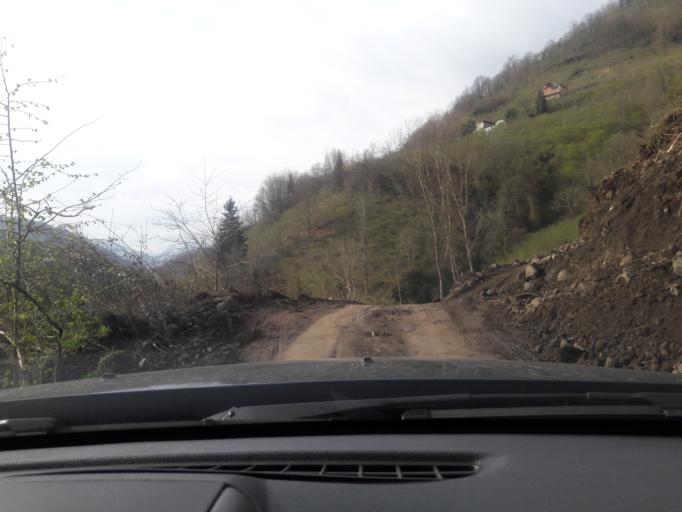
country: TR
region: Trabzon
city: Salpazari
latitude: 40.9688
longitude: 39.1957
